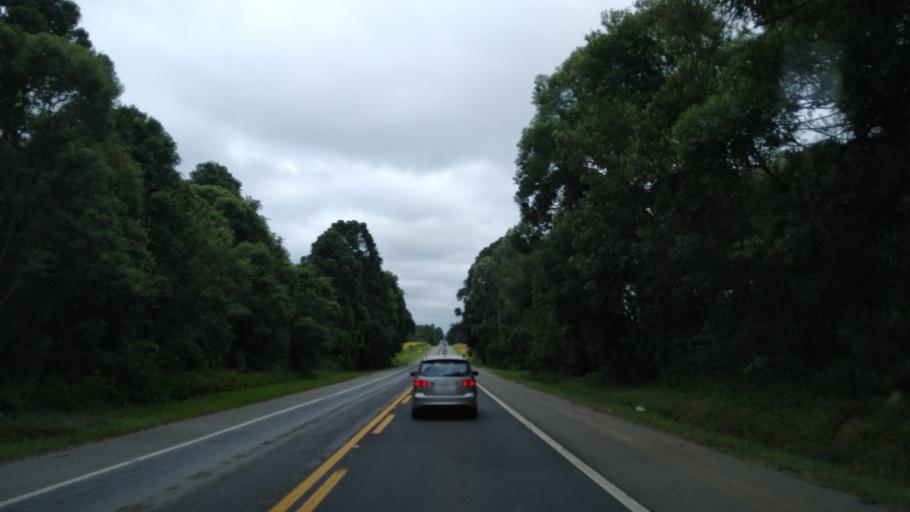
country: BR
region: Santa Catarina
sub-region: Tres Barras
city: Tres Barras
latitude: -26.1670
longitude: -50.1068
